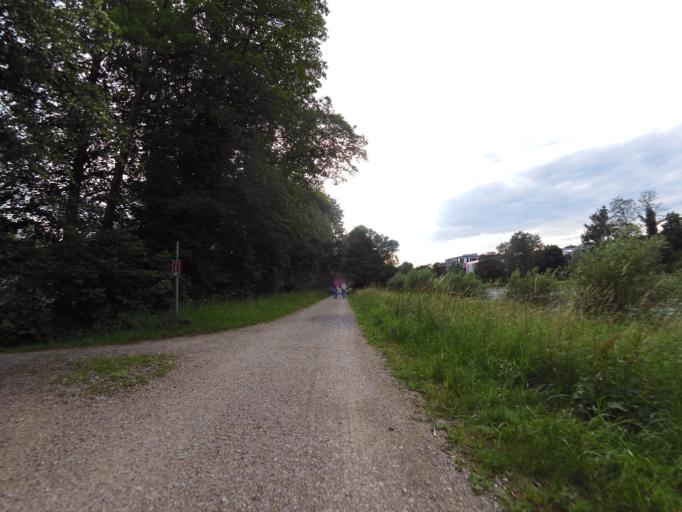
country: CH
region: Zurich
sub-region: Bezirk Dietikon
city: Dietikon / Schoenenwerd
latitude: 47.3996
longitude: 8.4284
